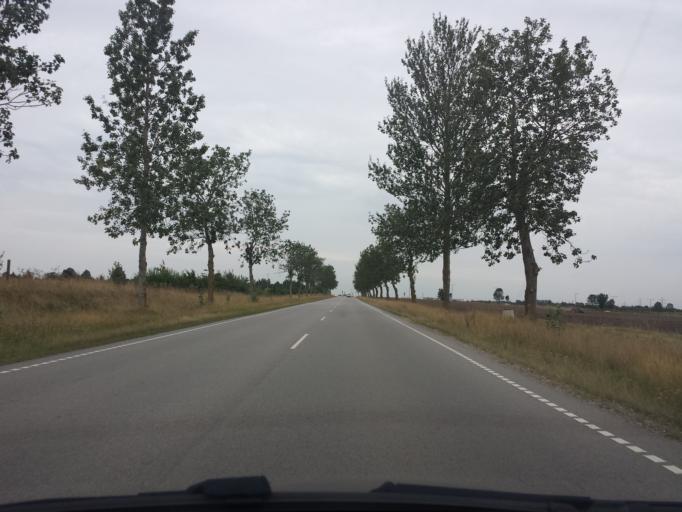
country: DK
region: Capital Region
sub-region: Hoje-Taastrup Kommune
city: Taastrup
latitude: 55.6578
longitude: 12.2534
